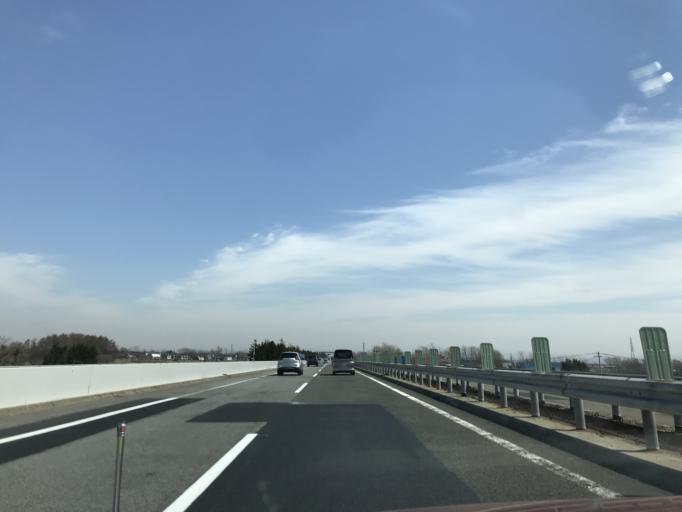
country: JP
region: Hokkaido
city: Ebetsu
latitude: 43.0954
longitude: 141.5813
